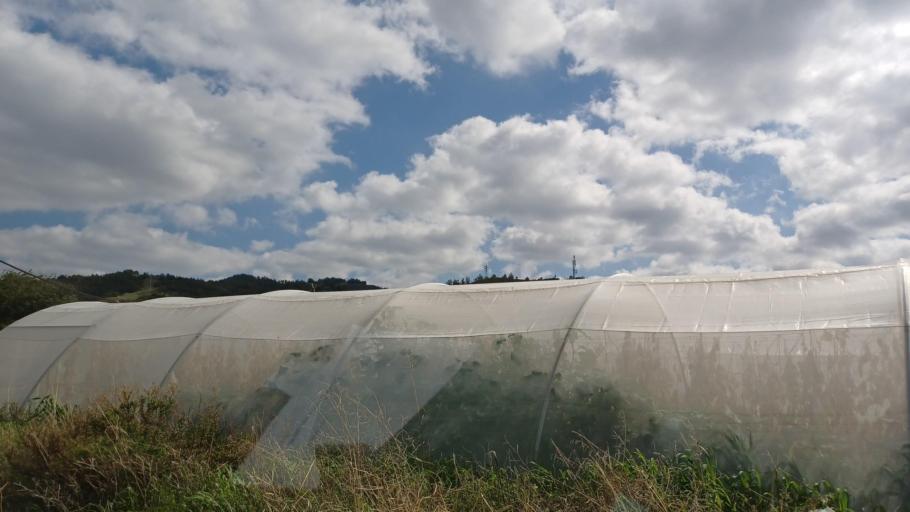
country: CY
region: Pafos
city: Polis
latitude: 35.1036
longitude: 32.5126
